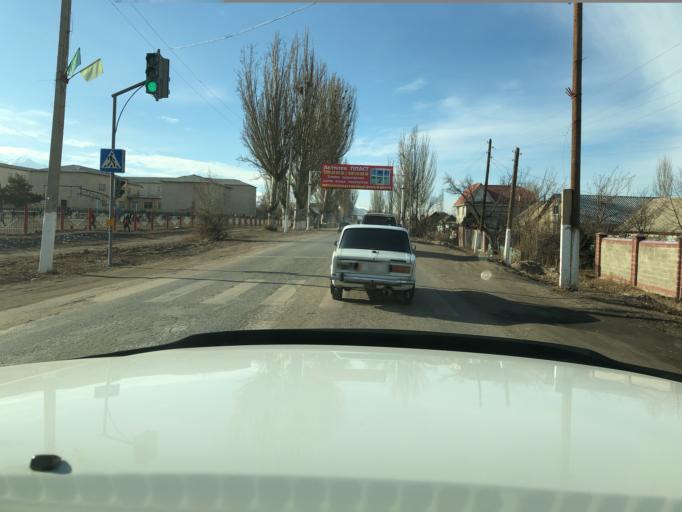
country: KG
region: Ysyk-Koel
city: Pokrovka
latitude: 42.3364
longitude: 77.9923
